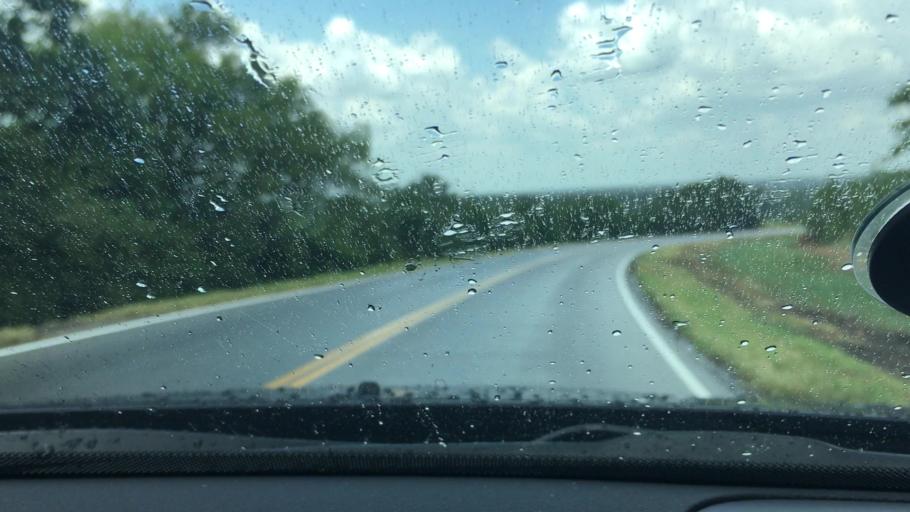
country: US
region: Oklahoma
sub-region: Johnston County
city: Tishomingo
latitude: 34.1885
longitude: -96.7241
